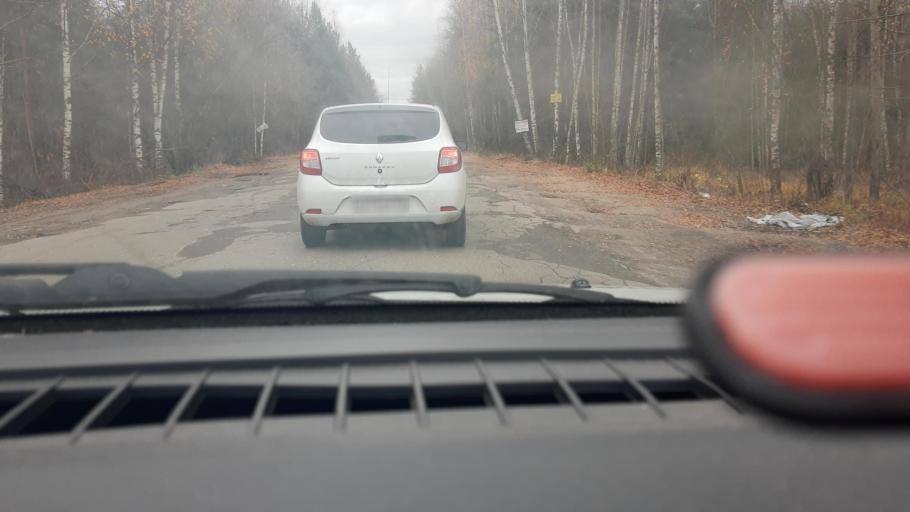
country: RU
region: Nizjnij Novgorod
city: Babino
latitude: 56.3048
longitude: 43.6615
